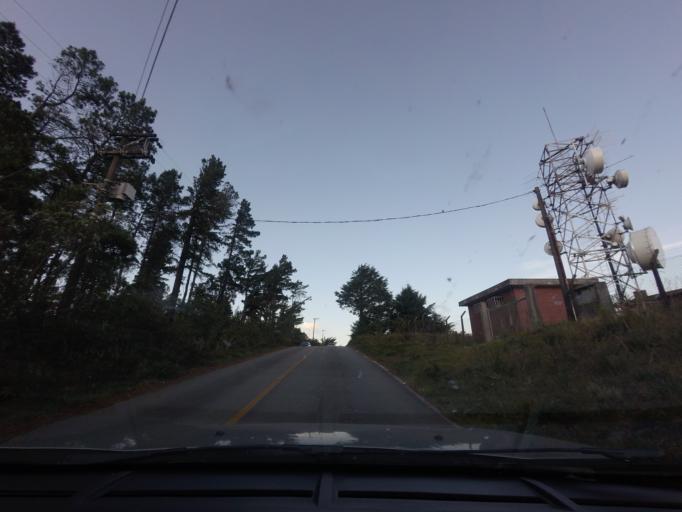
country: BR
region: Sao Paulo
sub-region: Campos Do Jordao
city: Campos do Jordao
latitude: -22.7686
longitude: -45.5259
